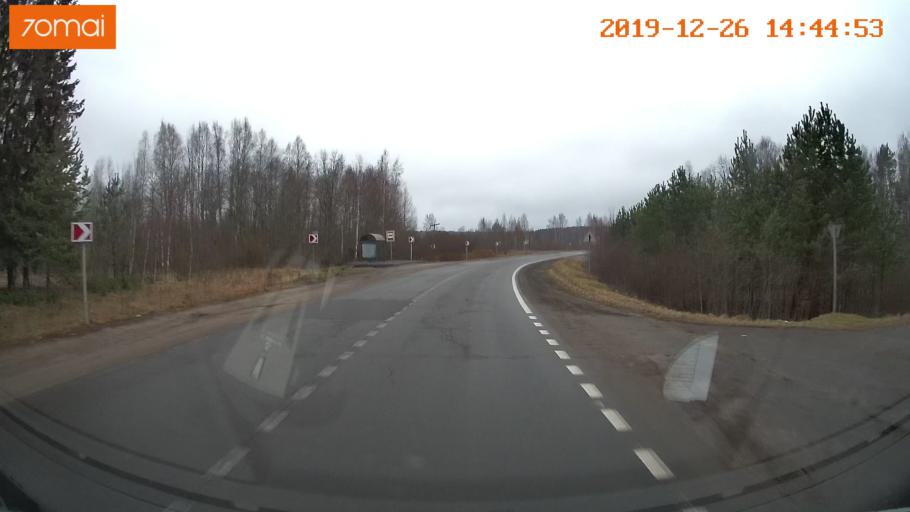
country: RU
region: Jaroslavl
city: Poshekhon'ye
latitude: 58.3421
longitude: 39.0498
